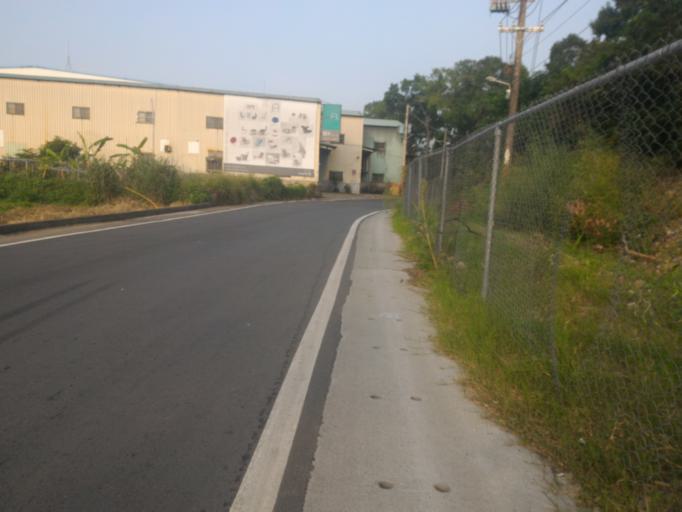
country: TW
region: Taiwan
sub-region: Taoyuan
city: Taoyuan
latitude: 24.9499
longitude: 121.3948
